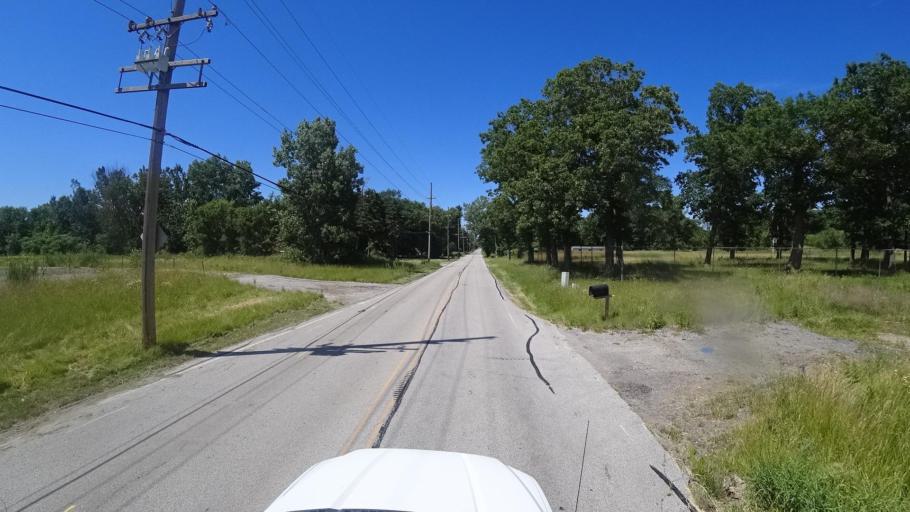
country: US
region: Indiana
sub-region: Porter County
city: Porter
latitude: 41.6335
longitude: -87.0673
